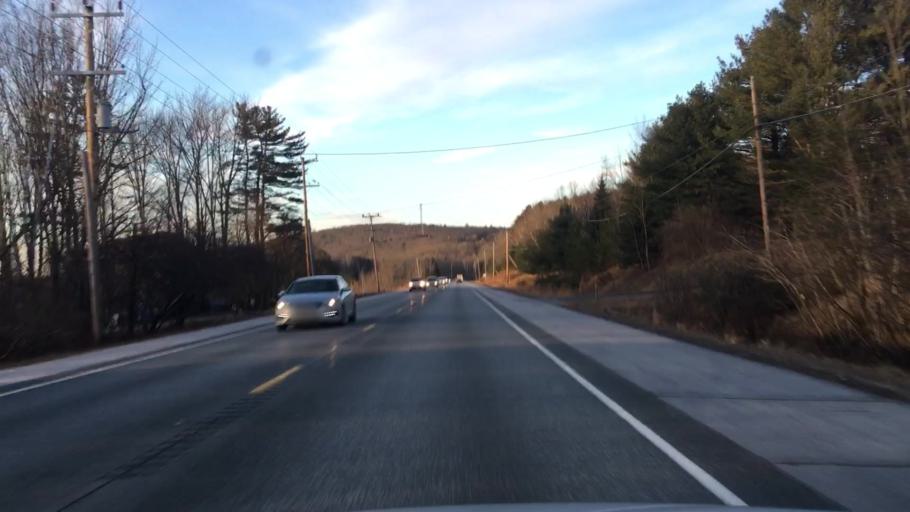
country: US
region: Maine
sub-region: Hancock County
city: Dedham
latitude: 44.7099
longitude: -68.6024
